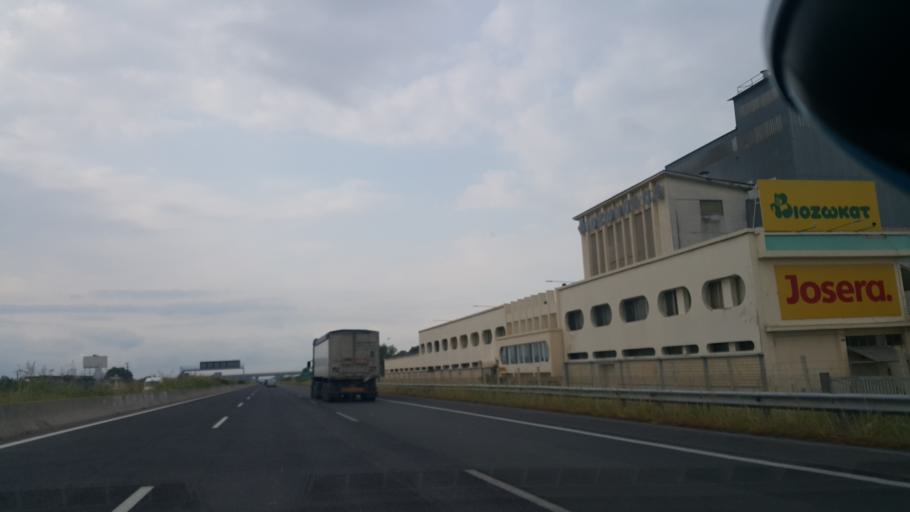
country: GR
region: Central Macedonia
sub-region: Nomos Pierias
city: Peristasi
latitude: 40.2481
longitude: 22.5336
